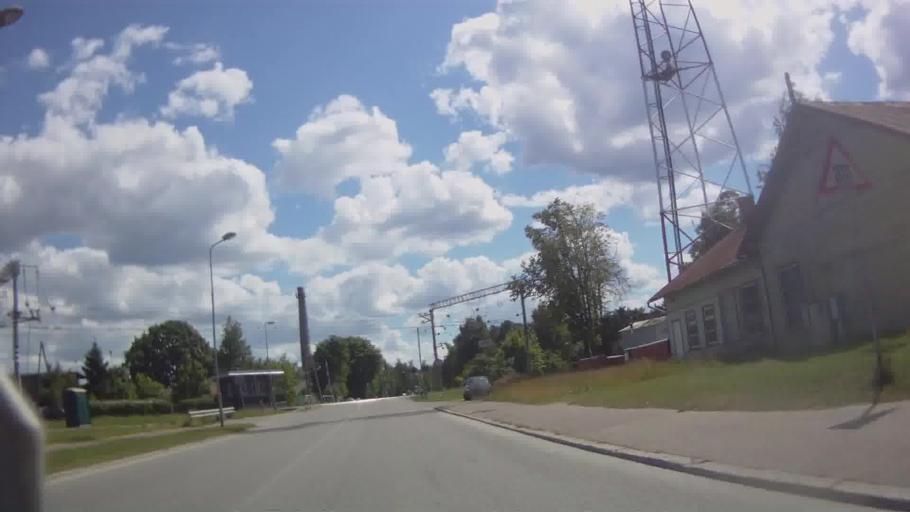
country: LV
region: Jurmala
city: Jurmala
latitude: 56.9645
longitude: 23.7714
